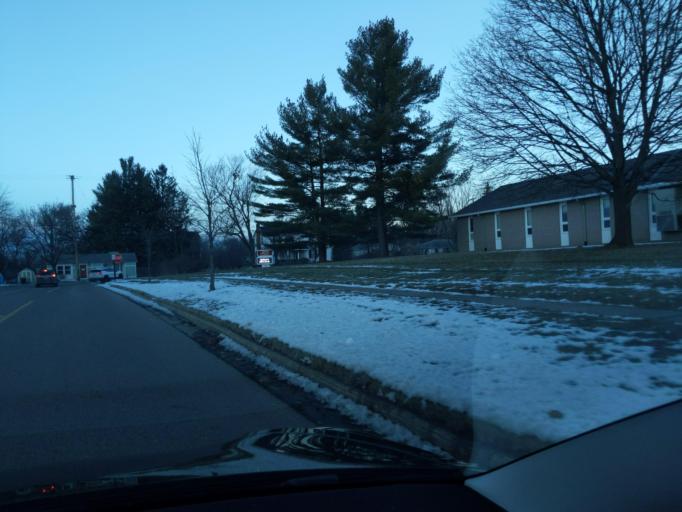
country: US
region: Michigan
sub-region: Ingham County
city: Mason
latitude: 42.5816
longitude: -84.4267
